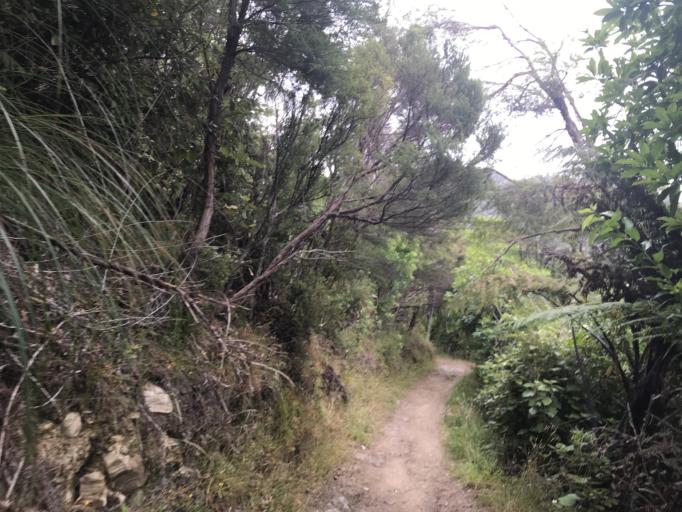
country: NZ
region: Marlborough
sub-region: Marlborough District
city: Picton
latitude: -41.2184
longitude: 173.9744
